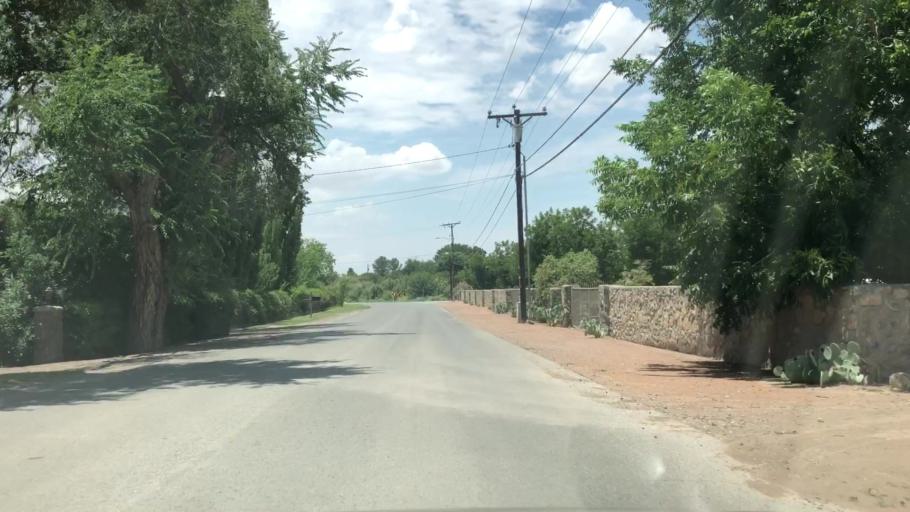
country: US
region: Texas
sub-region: El Paso County
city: Canutillo
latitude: 31.9090
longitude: -106.6335
